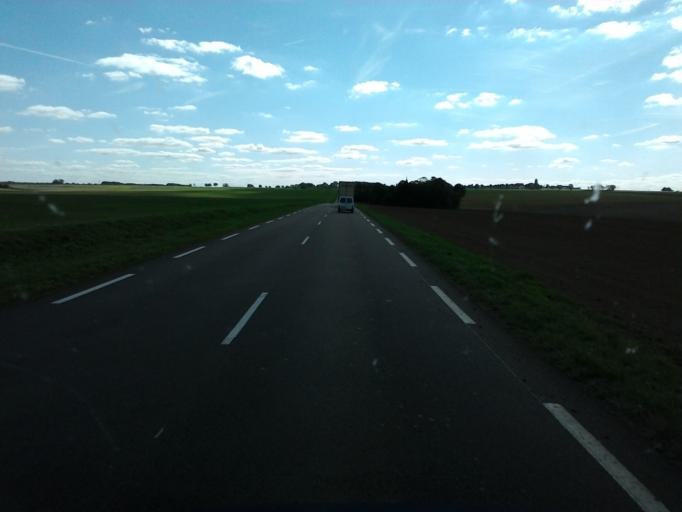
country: FR
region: Bourgogne
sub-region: Departement de la Cote-d'Or
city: Chatillon-sur-Seine
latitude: 47.7665
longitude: 4.5029
